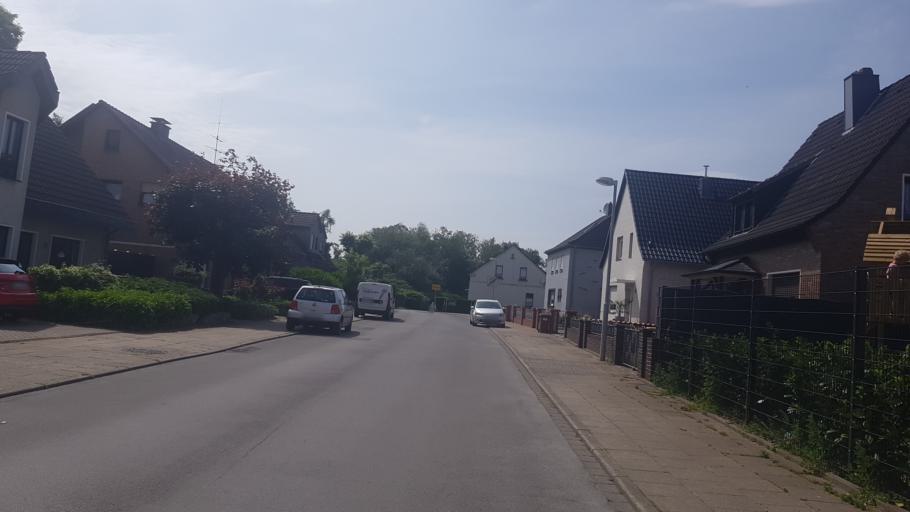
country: DE
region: North Rhine-Westphalia
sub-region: Regierungsbezirk Dusseldorf
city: Oberhausen
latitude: 51.4524
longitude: 6.8447
